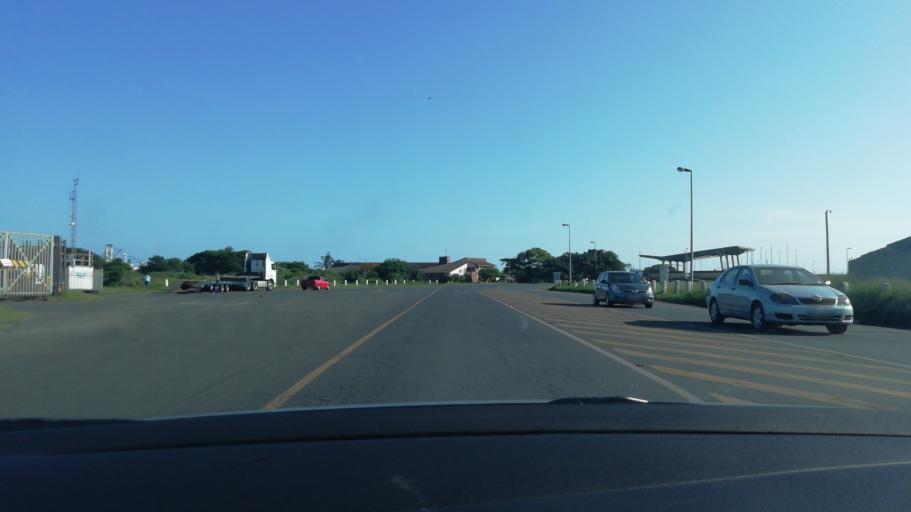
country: ZA
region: KwaZulu-Natal
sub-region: uThungulu District Municipality
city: Richards Bay
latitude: -28.7868
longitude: 32.0268
